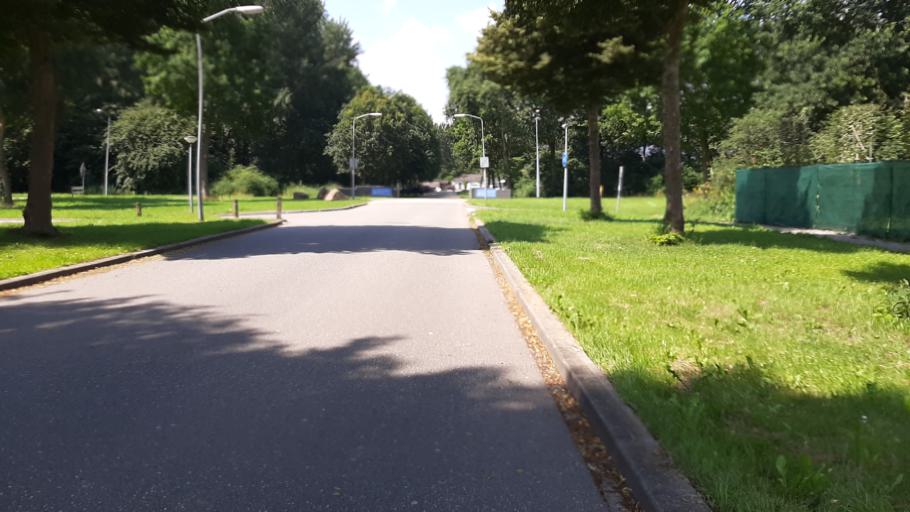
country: NL
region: Flevoland
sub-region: Gemeente Zeewolde
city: Zeewolde
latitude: 52.3224
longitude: 5.5319
